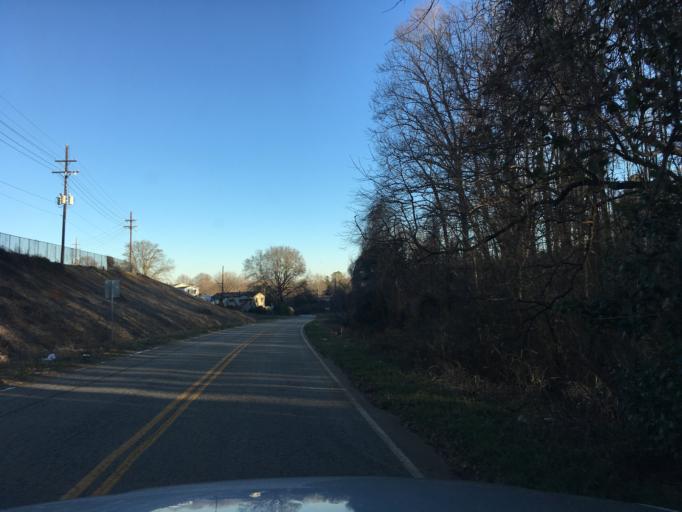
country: US
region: South Carolina
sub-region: Spartanburg County
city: Wellford
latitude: 34.9206
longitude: -82.1090
